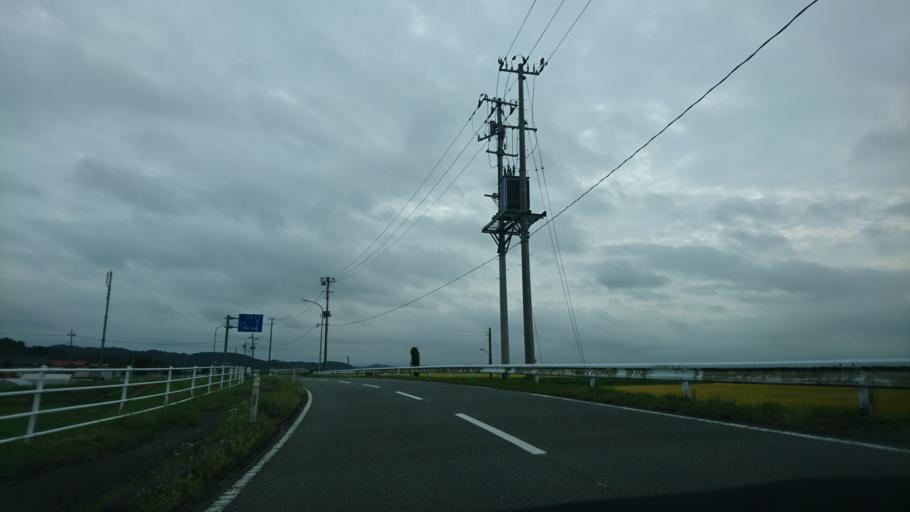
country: JP
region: Iwate
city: Ichinoseki
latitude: 38.8029
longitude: 141.1134
